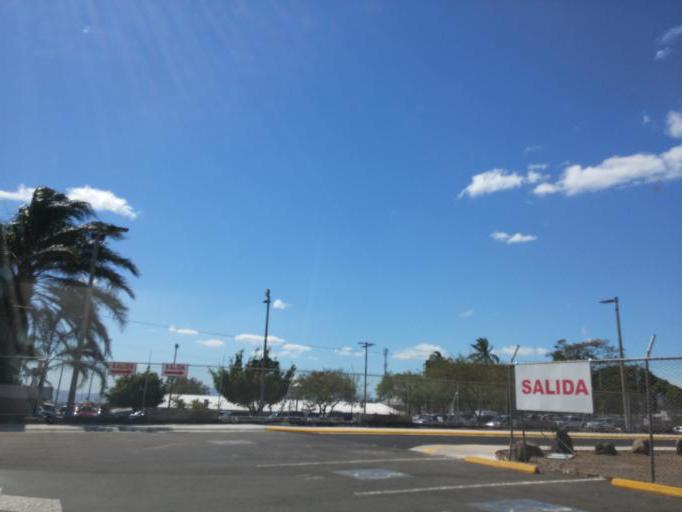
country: CR
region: Alajuela
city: Alajuela
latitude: 10.0131
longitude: -84.2221
